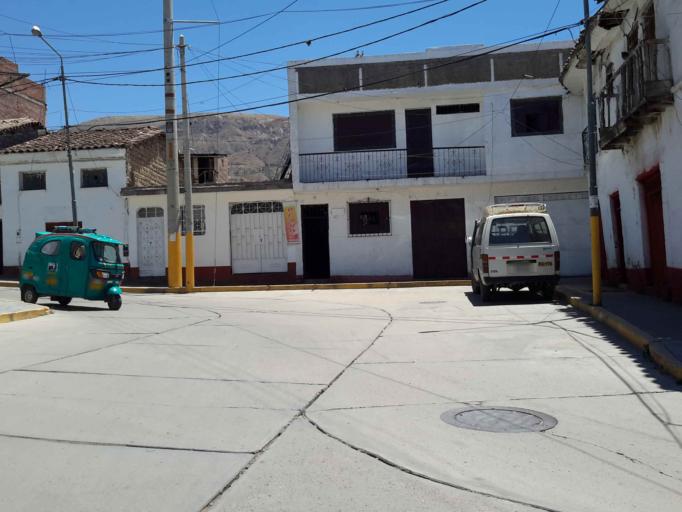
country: PE
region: Ayacucho
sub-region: Provincia de Huamanga
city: Ayacucho
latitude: -13.1657
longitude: -74.2237
